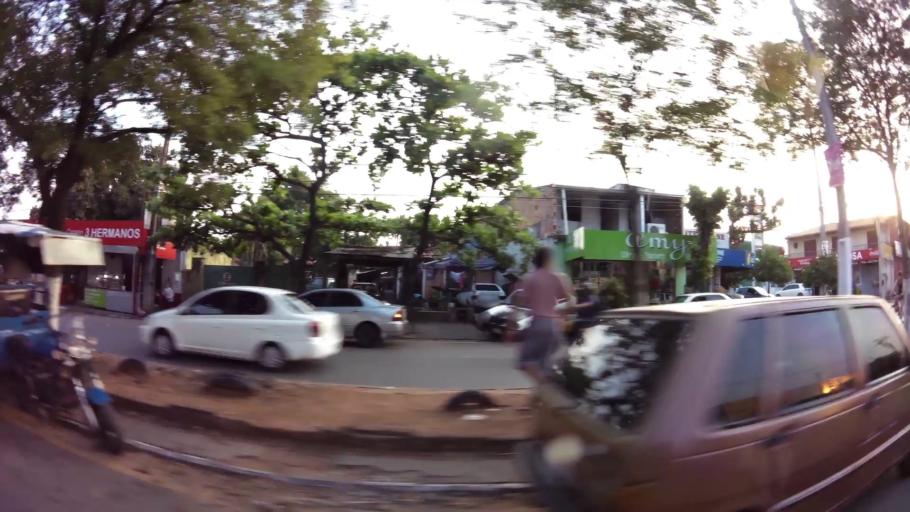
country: PY
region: Central
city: Lambare
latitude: -25.3562
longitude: -57.5993
